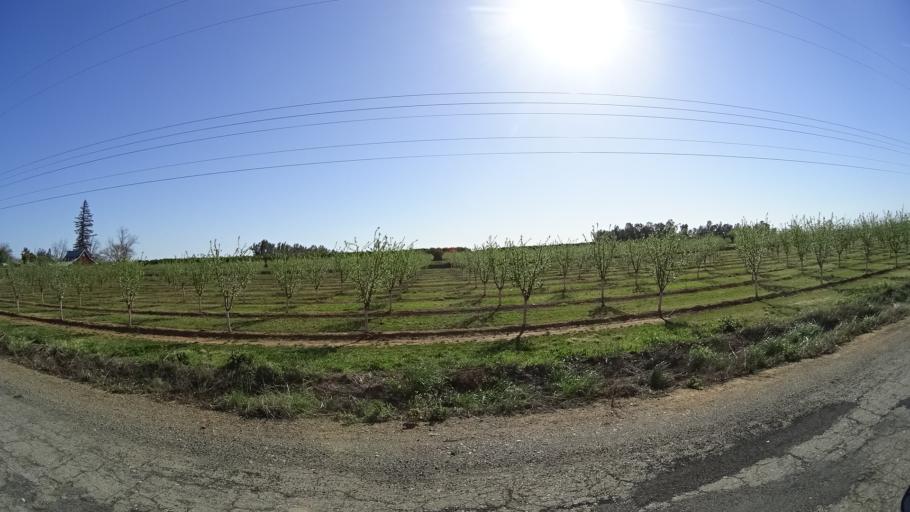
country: US
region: California
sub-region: Glenn County
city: Orland
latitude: 39.7353
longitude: -122.2482
